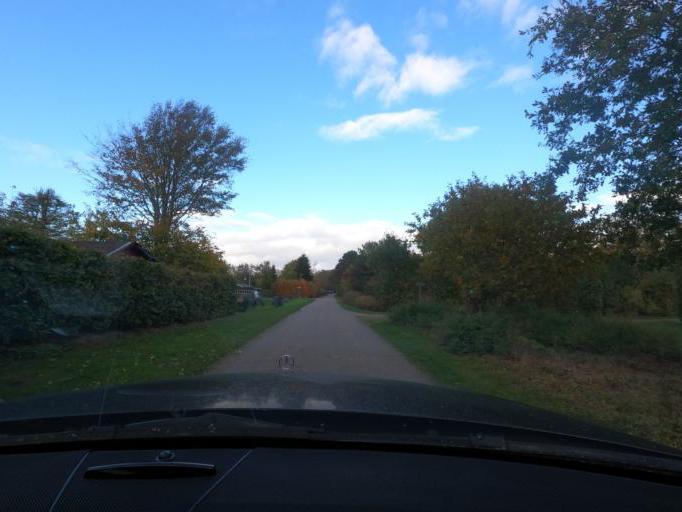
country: DK
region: South Denmark
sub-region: Sonderborg Kommune
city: Horuphav
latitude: 54.8676
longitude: 9.8905
